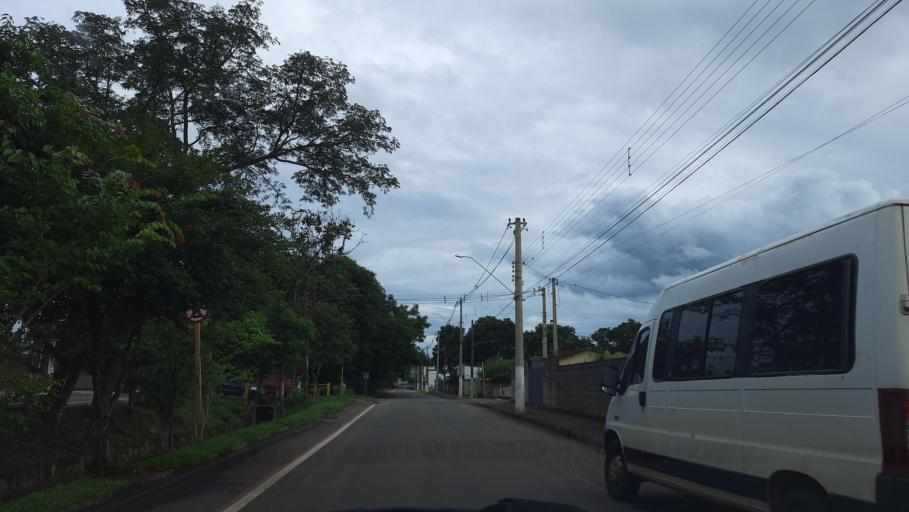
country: BR
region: Sao Paulo
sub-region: Casa Branca
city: Casa Branca
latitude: -21.7747
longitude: -47.0908
